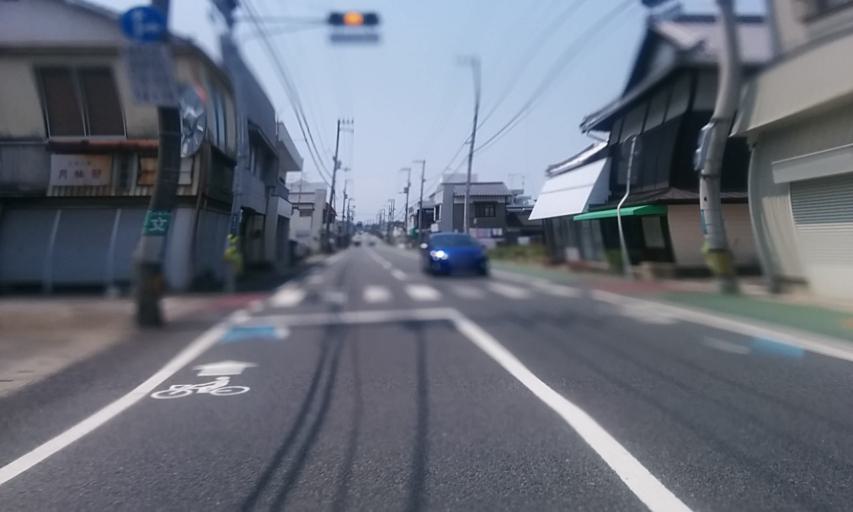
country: JP
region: Ehime
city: Niihama
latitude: 33.9233
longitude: 133.3057
